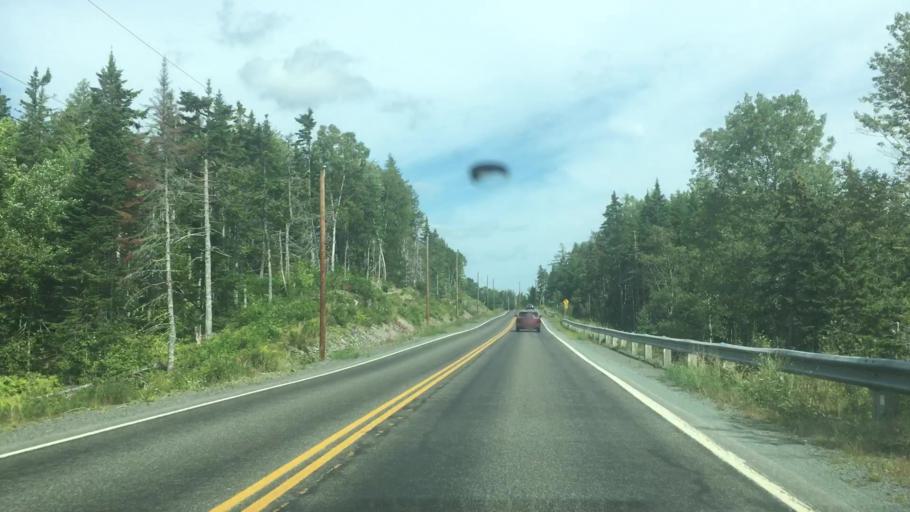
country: CA
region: Nova Scotia
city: Sydney Mines
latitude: 46.2100
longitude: -60.6215
